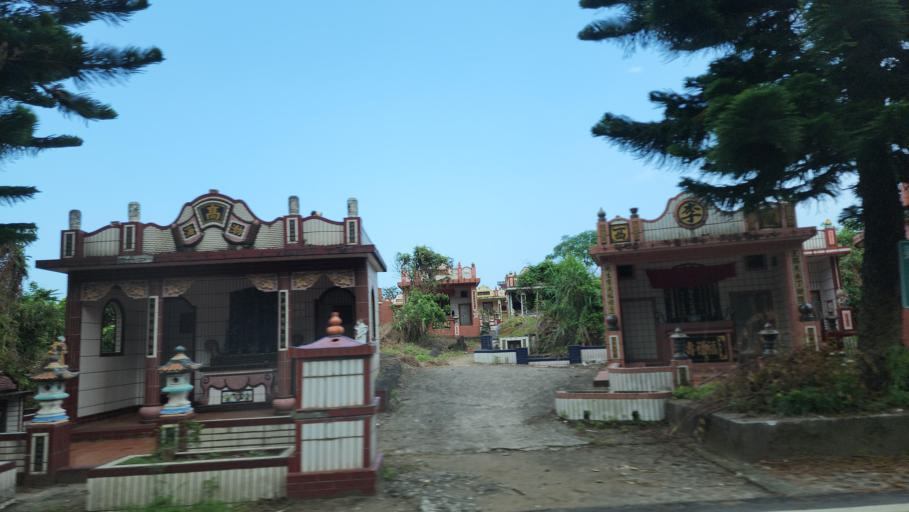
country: TW
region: Taiwan
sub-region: Keelung
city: Keelung
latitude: 25.2252
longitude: 121.6379
